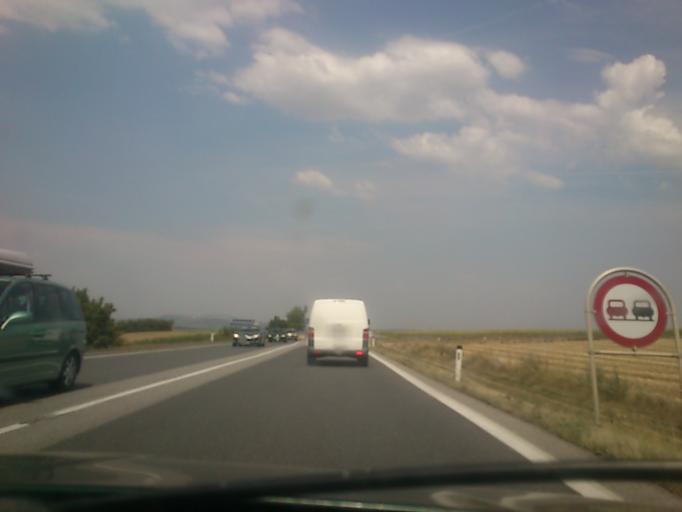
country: AT
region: Lower Austria
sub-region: Politischer Bezirk Mistelbach
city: Drasenhofen
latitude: 48.7125
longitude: 16.6540
